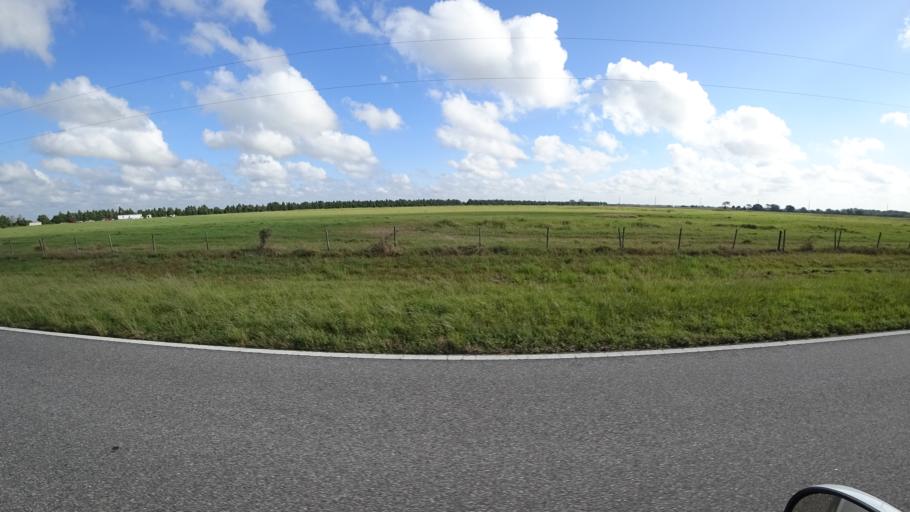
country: US
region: Florida
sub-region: Hillsborough County
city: Sun City Center
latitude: 27.5384
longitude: -82.3469
